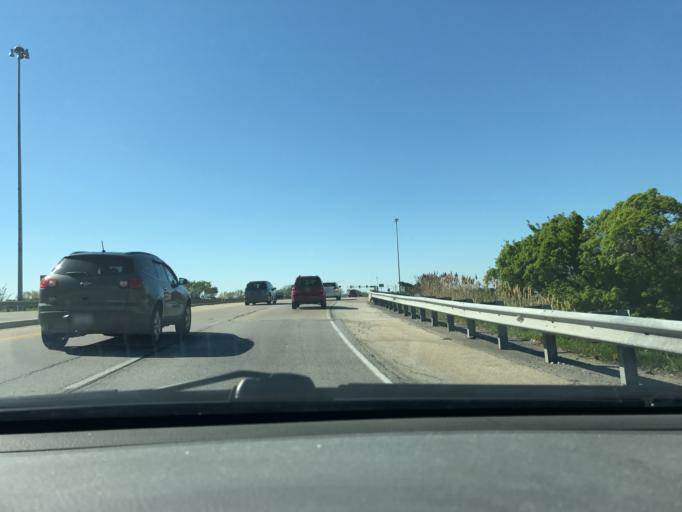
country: US
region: Illinois
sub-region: Kane County
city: Elgin
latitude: 42.0330
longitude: -88.3382
